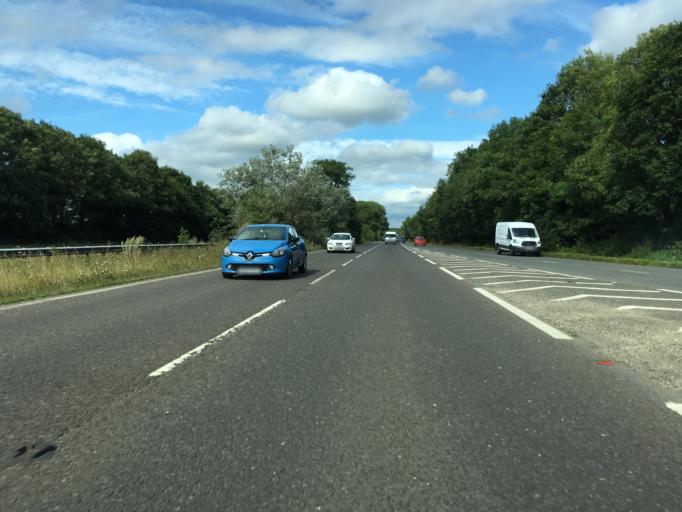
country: GB
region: England
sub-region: West Sussex
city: Horsham
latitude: 51.0718
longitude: -0.3489
